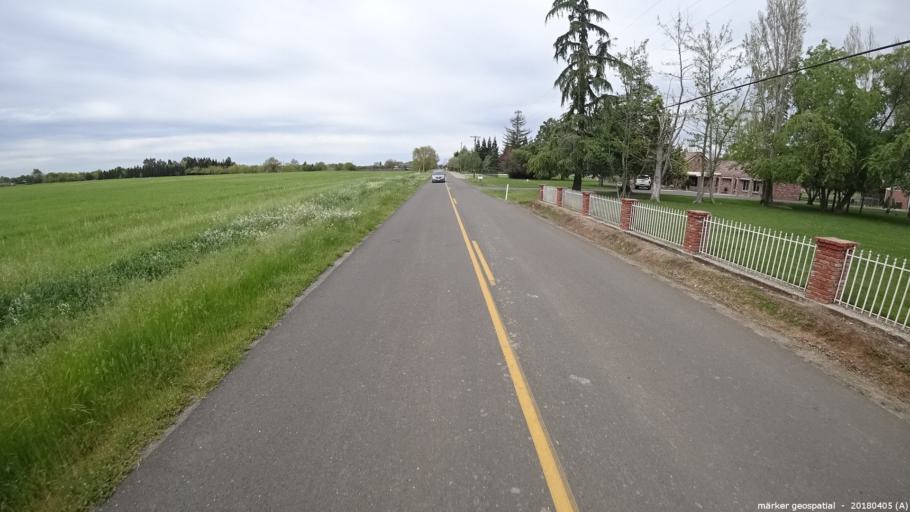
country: US
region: California
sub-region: Sacramento County
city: Galt
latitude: 38.2837
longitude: -121.3273
